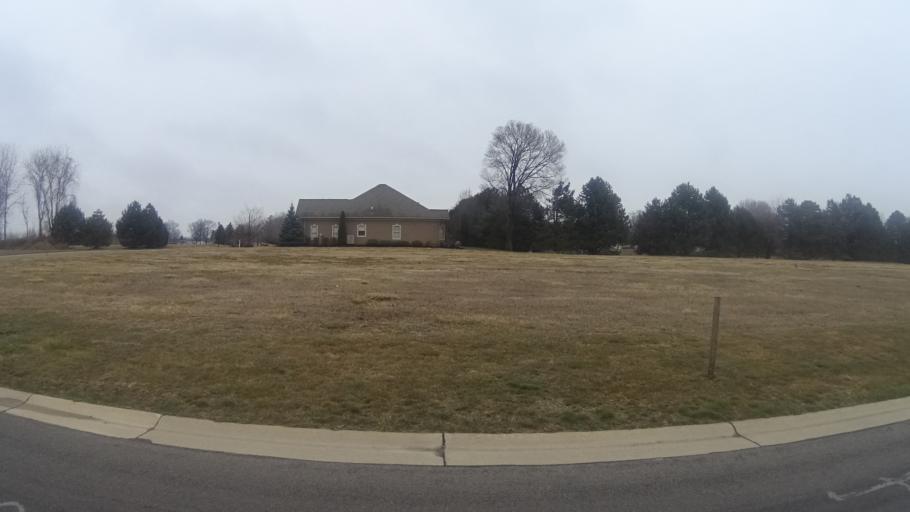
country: US
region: Ohio
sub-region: Erie County
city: Sandusky
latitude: 41.4201
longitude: -82.6550
